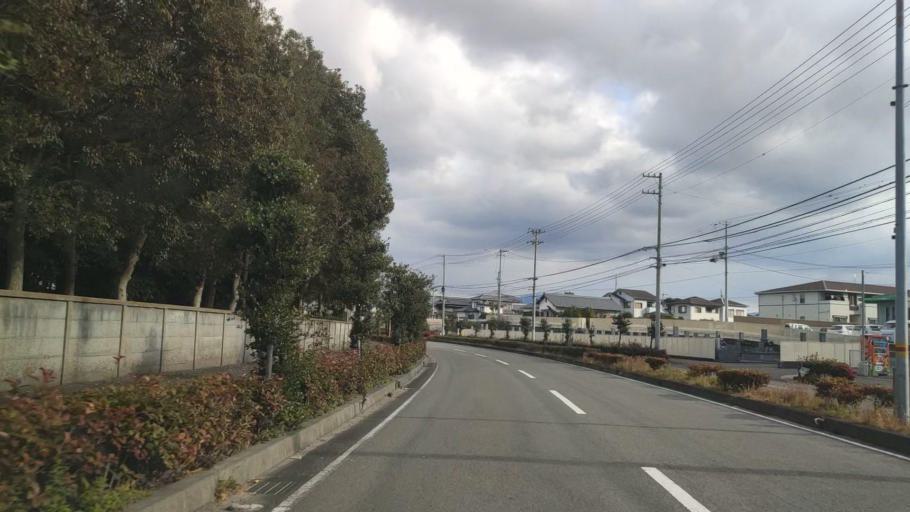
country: JP
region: Ehime
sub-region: Shikoku-chuo Shi
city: Matsuyama
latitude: 33.8475
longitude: 132.7124
